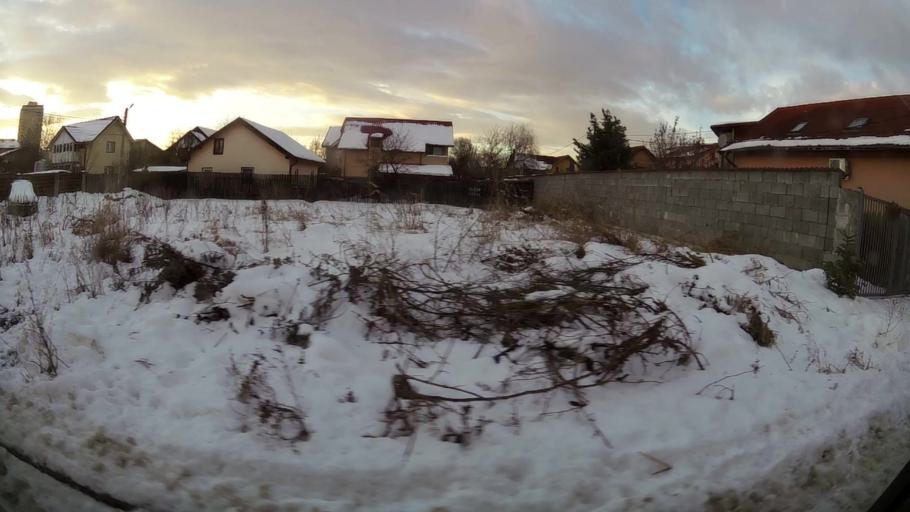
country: RO
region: Ilfov
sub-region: Comuna Popesti-Leordeni
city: Popesti-Leordeni
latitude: 44.3730
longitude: 26.1455
